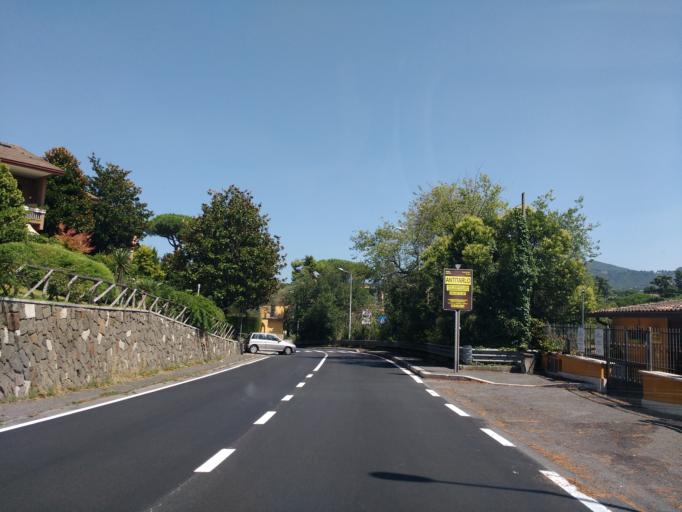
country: IT
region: Latium
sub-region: Citta metropolitana di Roma Capitale
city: Grottaferrata
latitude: 41.7829
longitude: 12.6812
